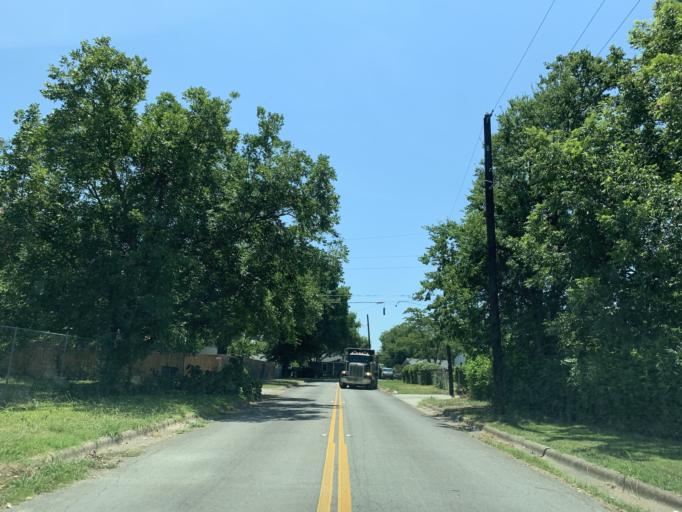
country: US
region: Texas
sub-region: Dallas County
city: Hutchins
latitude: 32.6790
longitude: -96.7607
